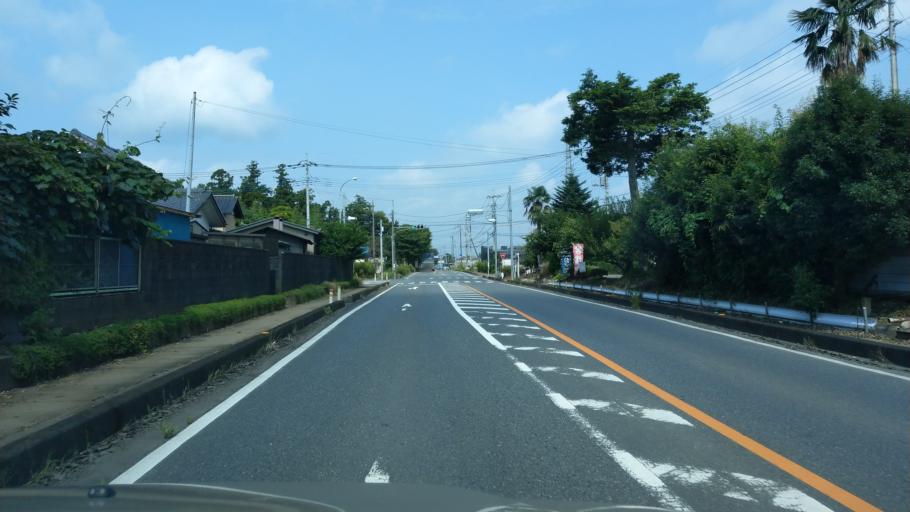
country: JP
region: Saitama
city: Sakado
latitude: 36.0158
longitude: 139.4235
